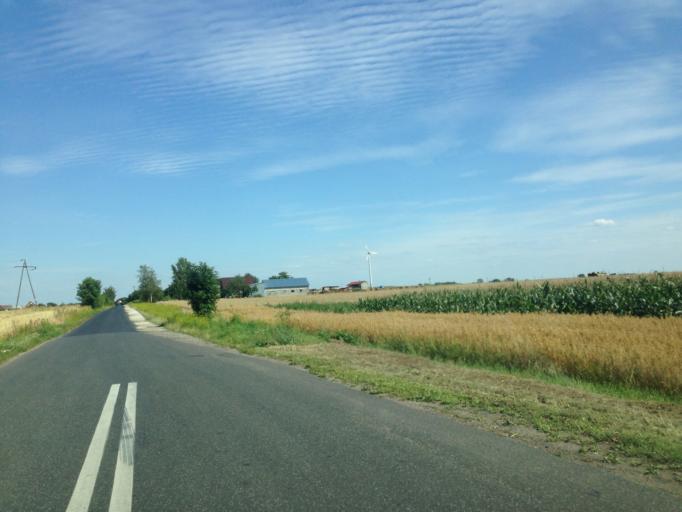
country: PL
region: Kujawsko-Pomorskie
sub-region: Powiat swiecki
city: Swiecie
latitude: 53.4665
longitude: 18.4401
